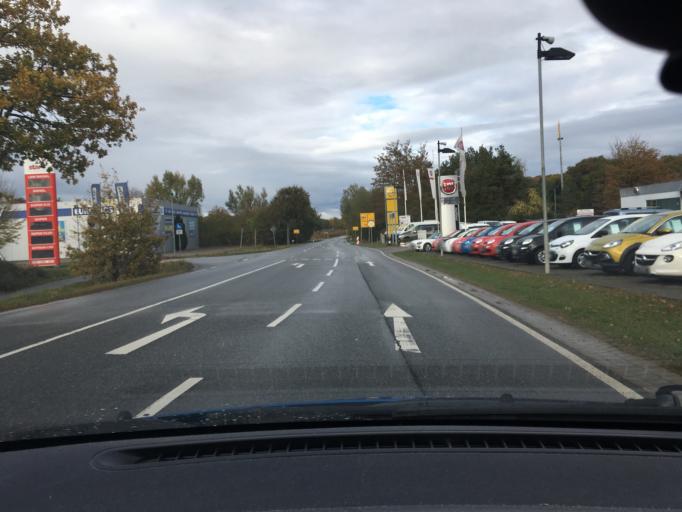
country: DE
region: Schleswig-Holstein
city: Molln
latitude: 53.6395
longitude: 10.6959
